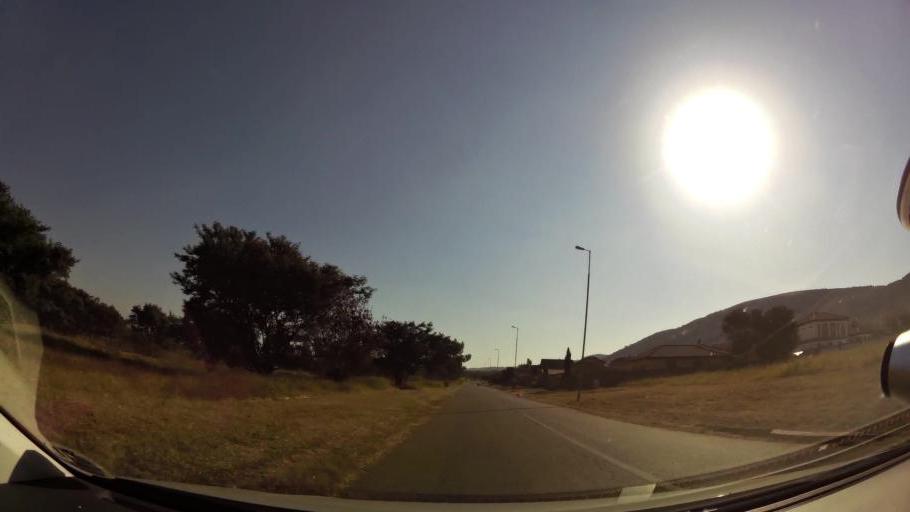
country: ZA
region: Gauteng
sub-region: City of Tshwane Metropolitan Municipality
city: Pretoria
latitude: -25.6960
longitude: 28.1341
